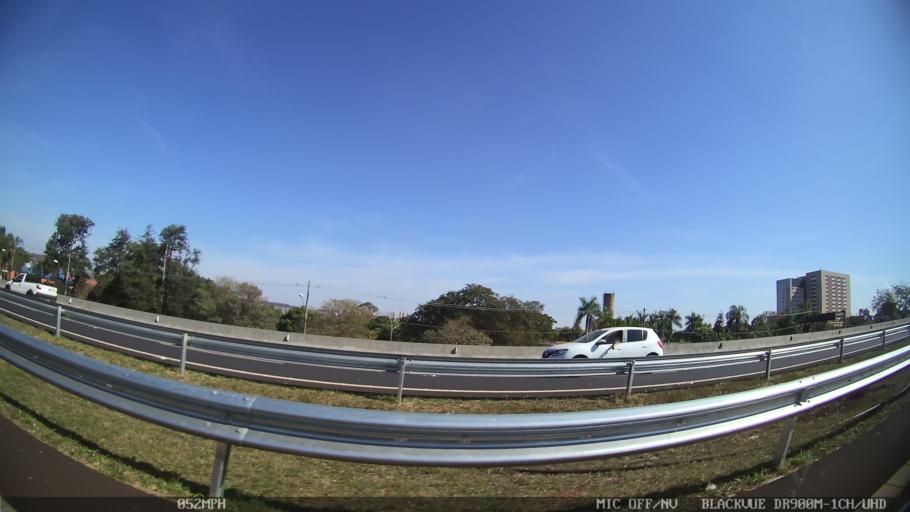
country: BR
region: Sao Paulo
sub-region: Ribeirao Preto
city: Ribeirao Preto
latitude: -21.2012
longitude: -47.7651
